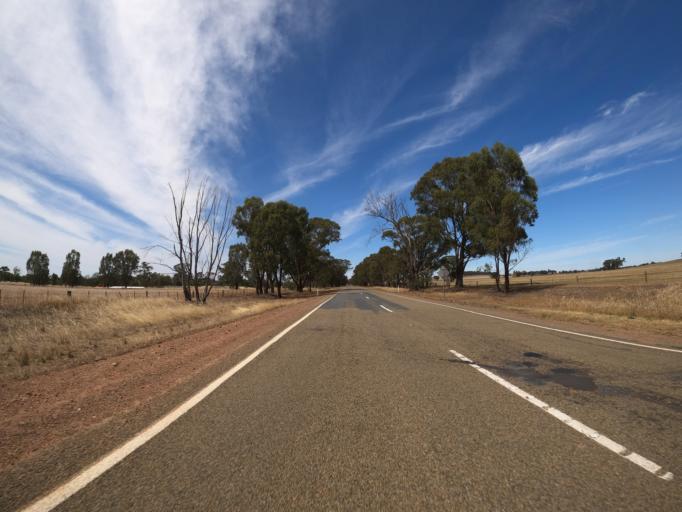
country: AU
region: Victoria
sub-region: Benalla
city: Benalla
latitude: -36.3086
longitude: 145.9583
